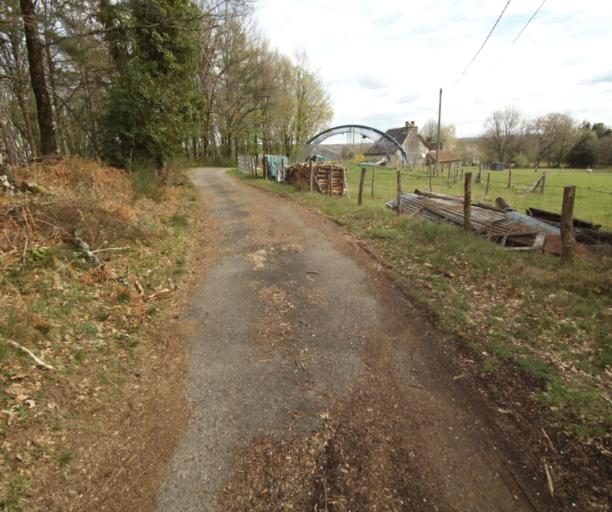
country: FR
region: Limousin
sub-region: Departement de la Correze
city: Argentat
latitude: 45.1808
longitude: 1.9375
